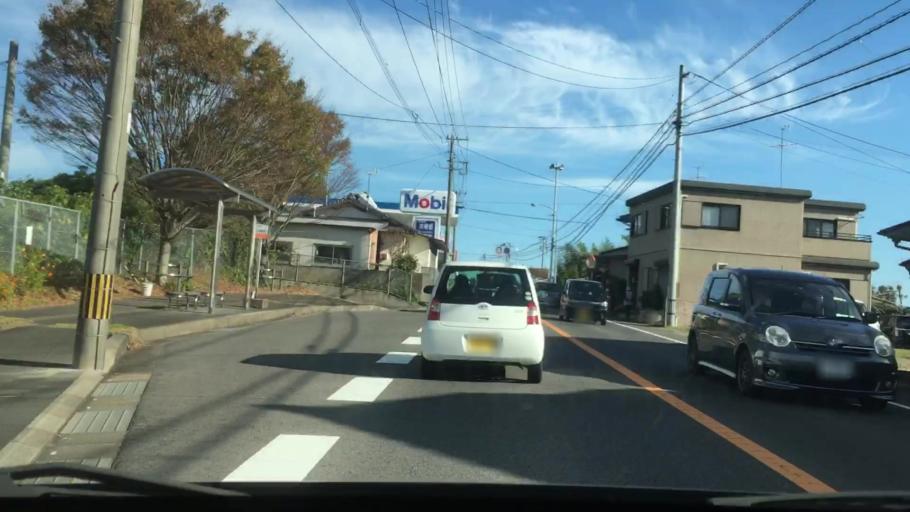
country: JP
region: Nagasaki
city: Sasebo
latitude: 33.0576
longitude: 129.7620
